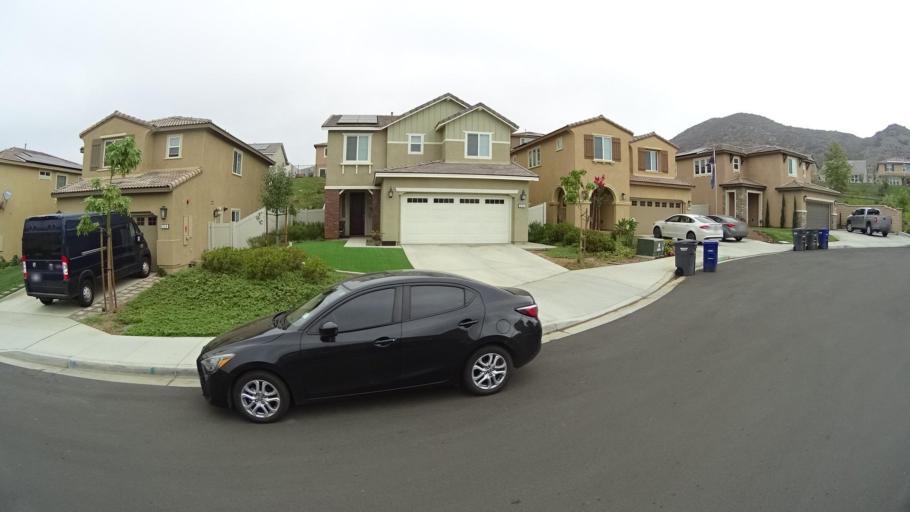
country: US
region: California
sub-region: San Diego County
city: Rainbow
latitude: 33.3560
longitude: -117.1530
